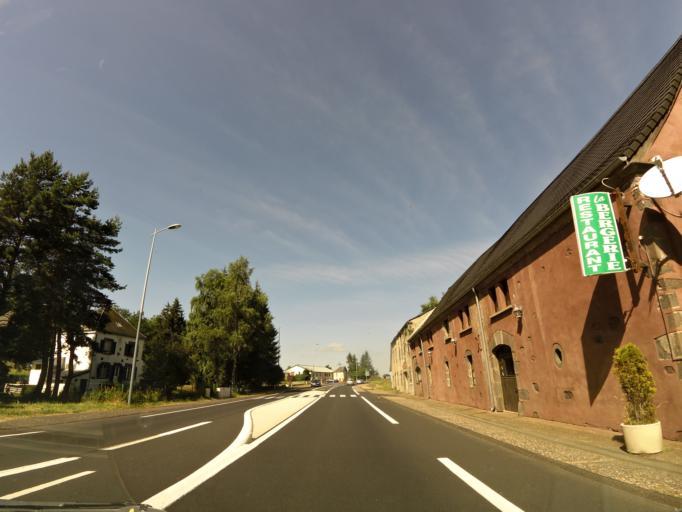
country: FR
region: Auvergne
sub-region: Departement du Puy-de-Dome
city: Aydat
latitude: 45.6853
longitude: 2.9405
